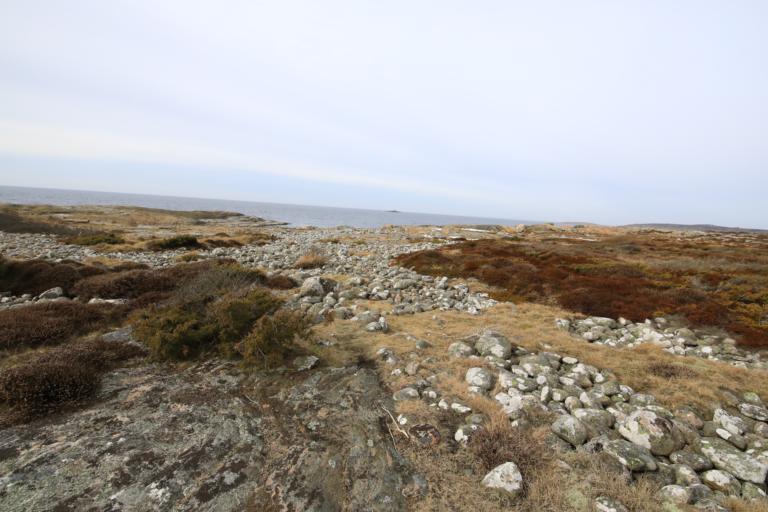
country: SE
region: Halland
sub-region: Kungsbacka Kommun
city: Frillesas
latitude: 57.2366
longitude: 12.0960
